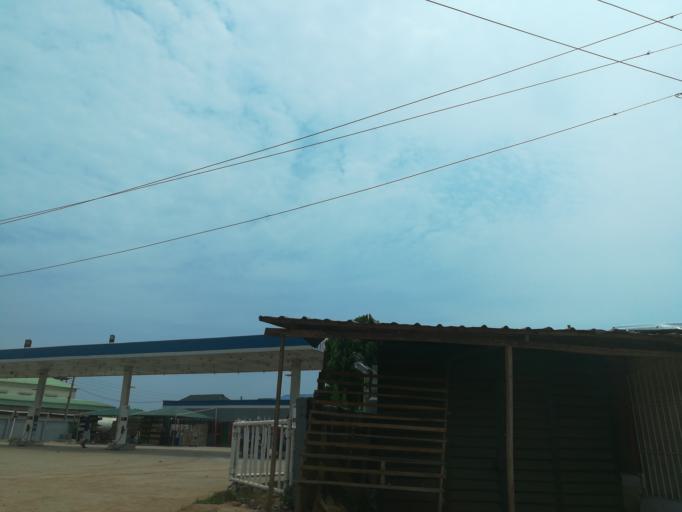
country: NG
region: Lagos
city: Ikorodu
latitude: 6.6080
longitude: 3.5918
